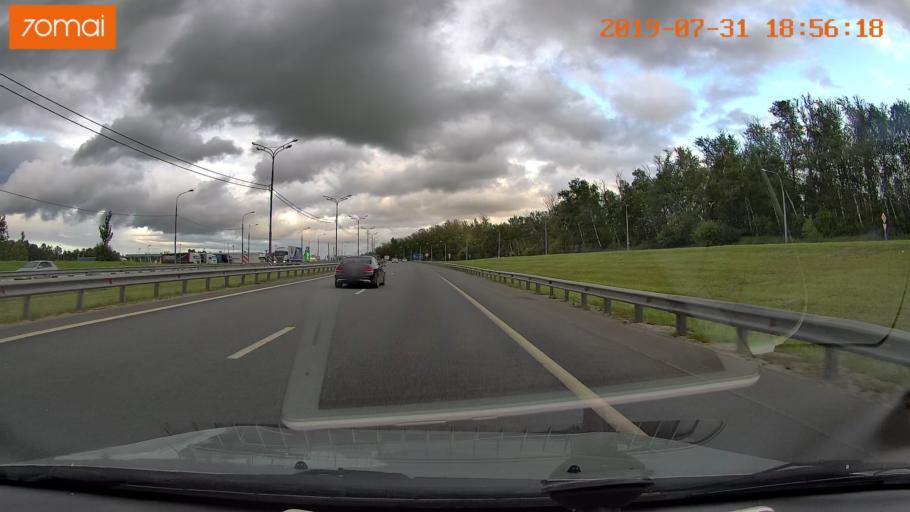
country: RU
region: Moskovskaya
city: Raduzhnyy
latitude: 55.1647
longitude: 38.6758
